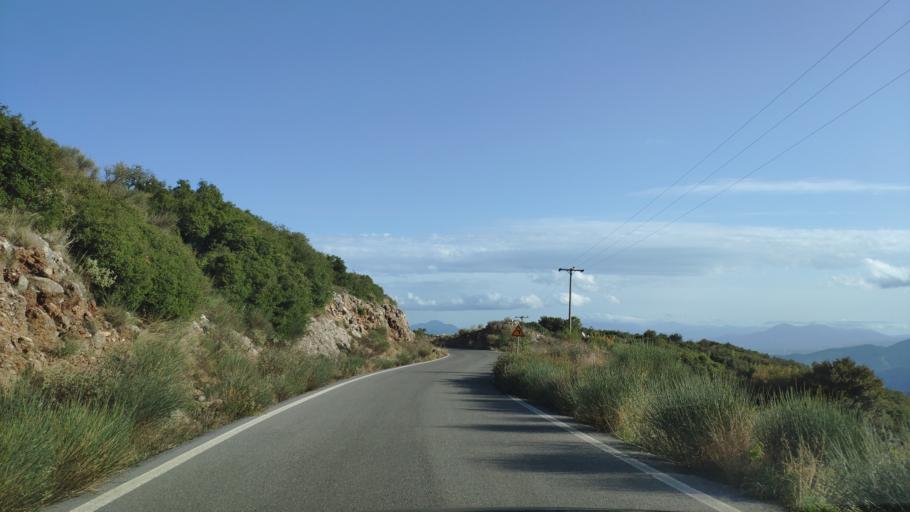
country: GR
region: Peloponnese
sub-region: Nomos Arkadias
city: Dimitsana
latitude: 37.5675
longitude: 22.0230
